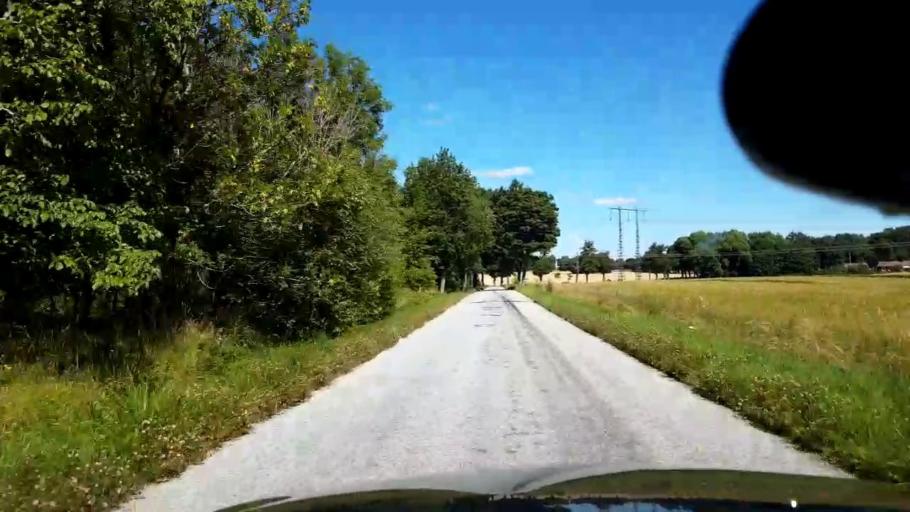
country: SE
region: Stockholm
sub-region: Upplands-Bro Kommun
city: Bro
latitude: 59.5969
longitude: 17.6423
